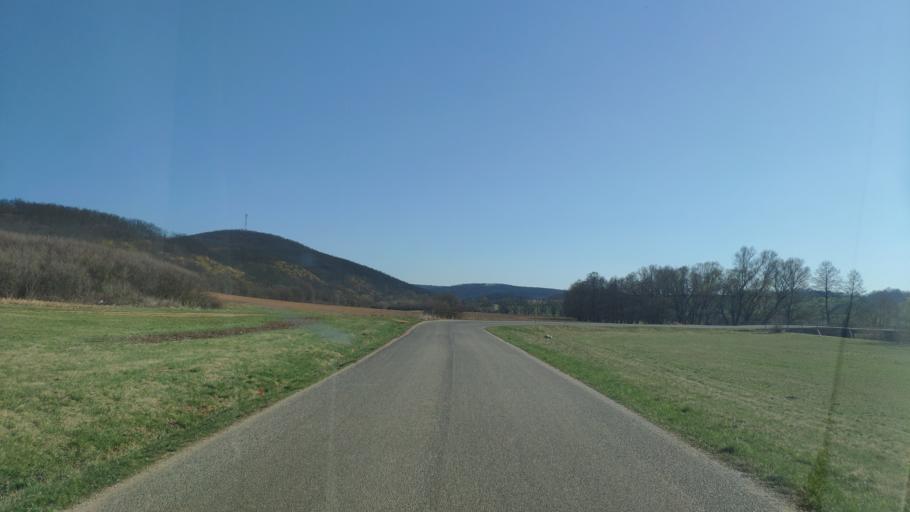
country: SK
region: Banskobystricky
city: Revuca
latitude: 48.5405
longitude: 20.3033
